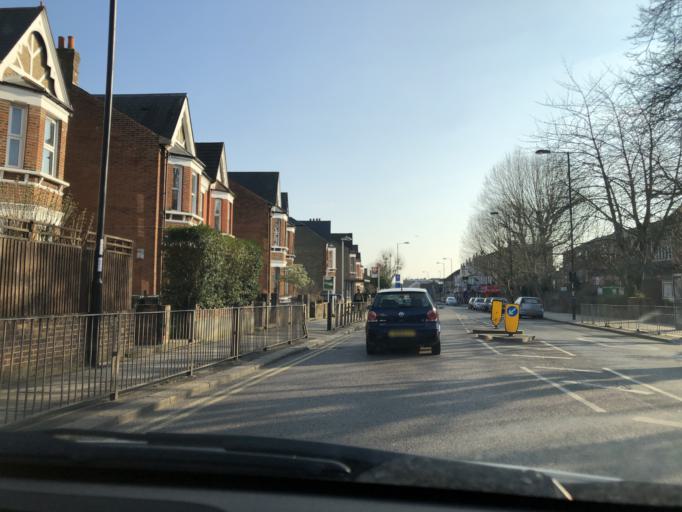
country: GB
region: England
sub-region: Greater London
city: Catford
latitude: 51.4455
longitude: -0.0426
